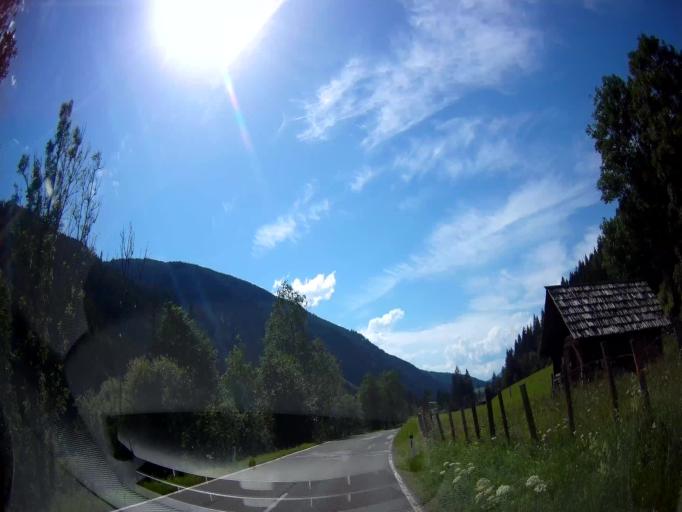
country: AT
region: Salzburg
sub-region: Politischer Bezirk Tamsweg
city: Thomatal
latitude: 47.0641
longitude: 13.7698
